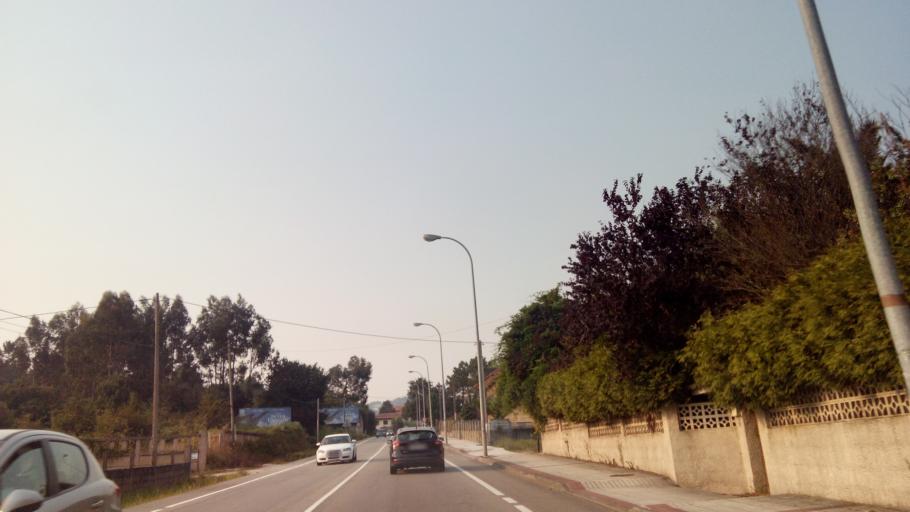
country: ES
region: Galicia
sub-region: Provincia de Pontevedra
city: Nigran
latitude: 42.1347
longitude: -8.8082
